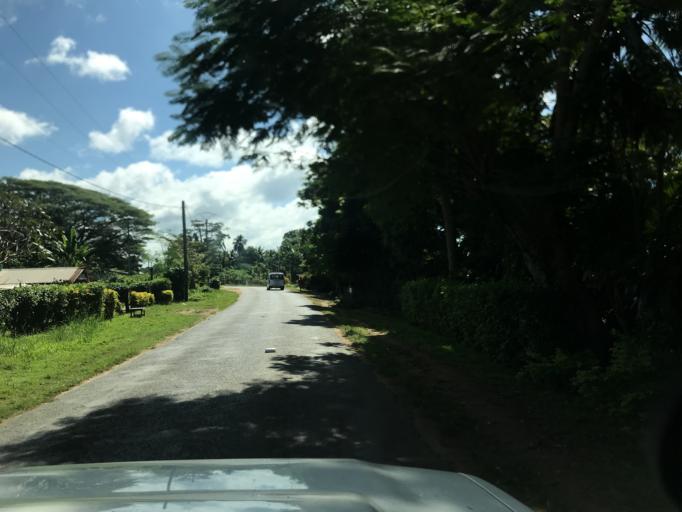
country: VU
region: Sanma
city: Luganville
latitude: -15.5286
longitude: 167.1546
